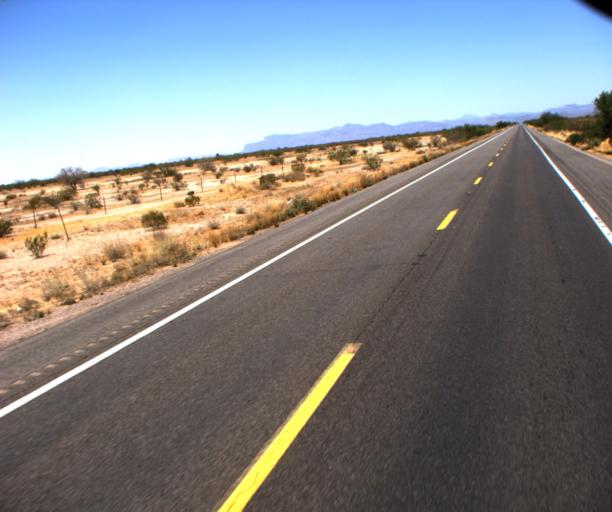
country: US
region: Arizona
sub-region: Pinal County
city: Florence
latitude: 33.1480
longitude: -111.3569
